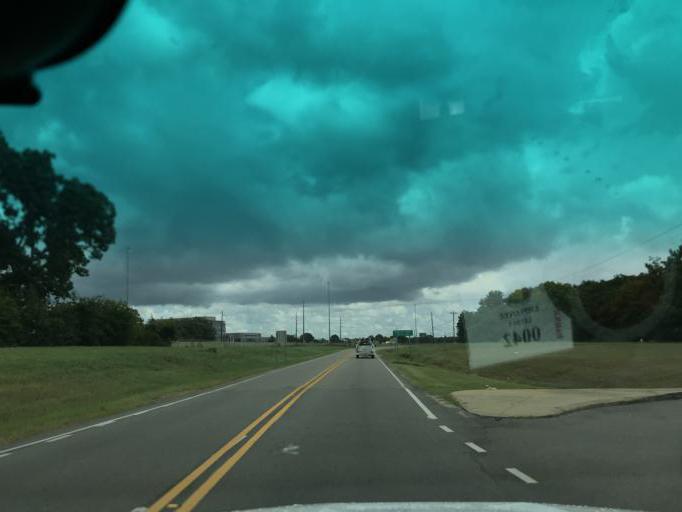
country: US
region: Alabama
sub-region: Montgomery County
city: Pike Road
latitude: 32.3670
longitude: -86.1361
